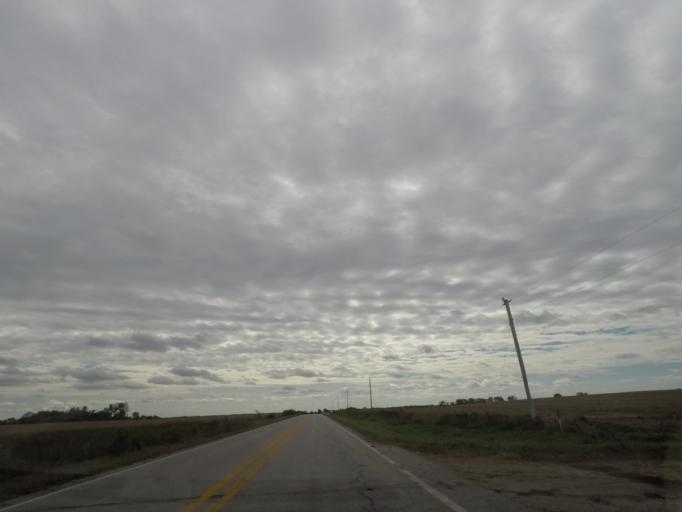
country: US
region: Iowa
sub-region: Story County
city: Huxley
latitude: 41.8613
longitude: -93.5316
